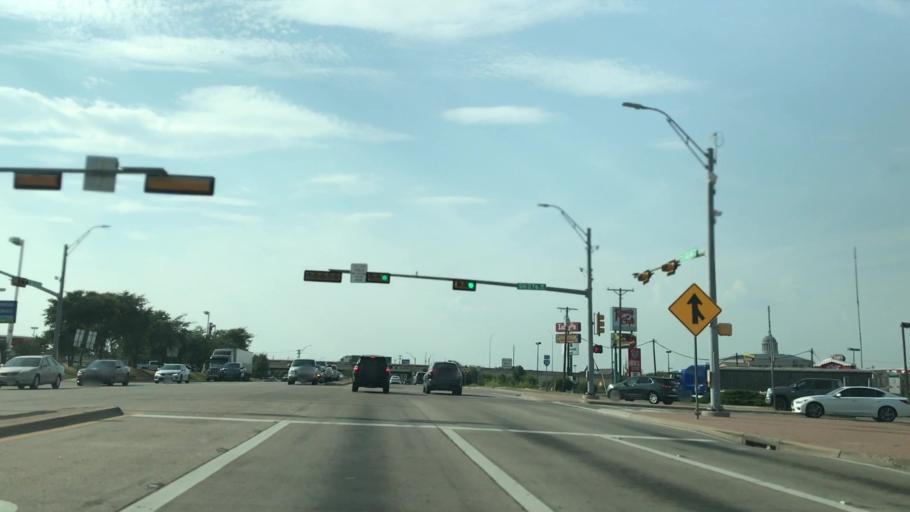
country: US
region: Texas
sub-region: Rockwall County
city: Rockwall
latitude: 32.9067
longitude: -96.4483
